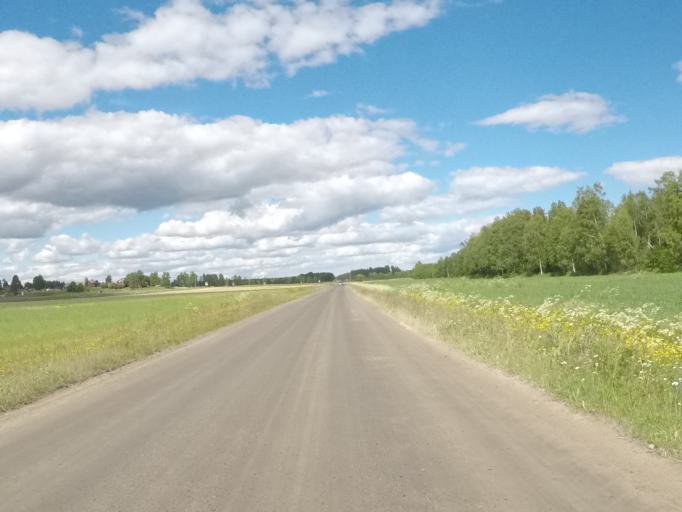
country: SE
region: Vaesterbotten
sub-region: Robertsfors Kommun
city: Robertsfors
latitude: 64.0737
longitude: 20.8654
